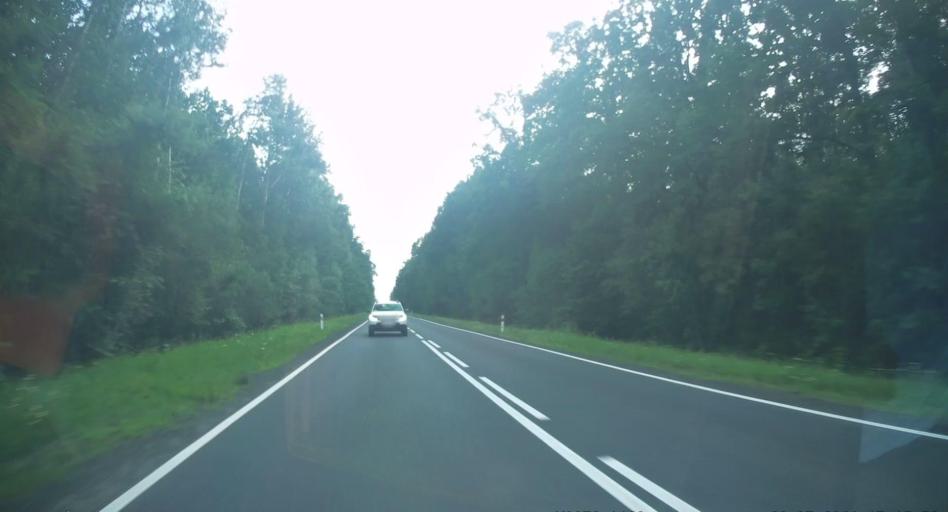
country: PL
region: Silesian Voivodeship
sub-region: Powiat czestochowski
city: Klomnice
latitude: 50.9541
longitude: 19.4014
